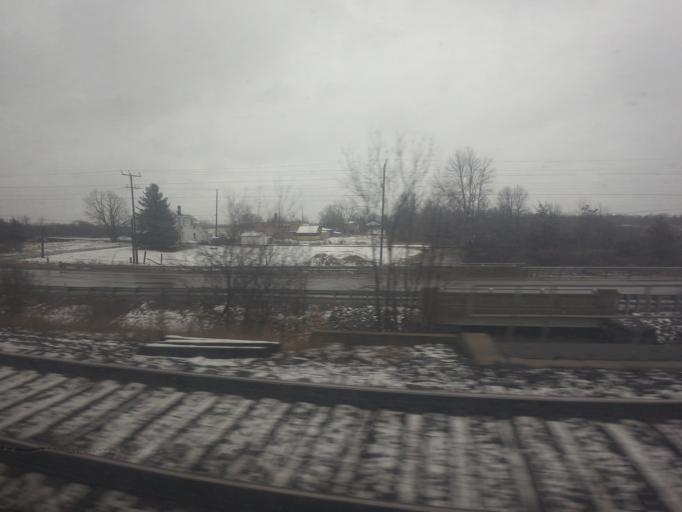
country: CA
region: Ontario
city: Belleville
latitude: 44.1635
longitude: -77.4294
